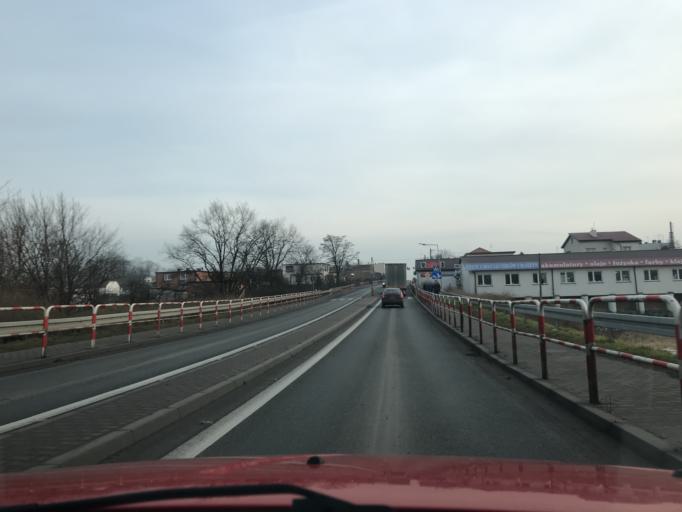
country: PL
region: Greater Poland Voivodeship
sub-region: Powiat ostrowski
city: Nowe Skalmierzyce
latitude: 51.7864
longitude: 18.0082
